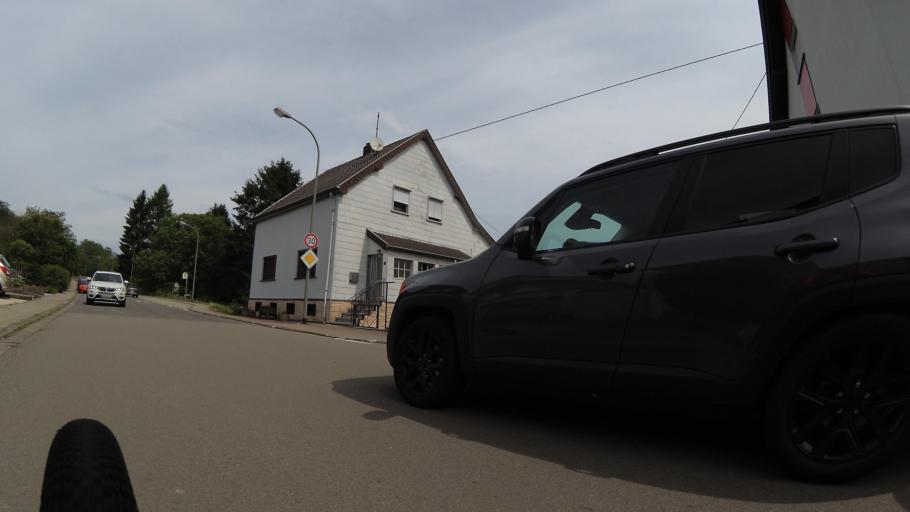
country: DE
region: Saarland
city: Merchweiler
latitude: 49.3352
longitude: 7.0554
